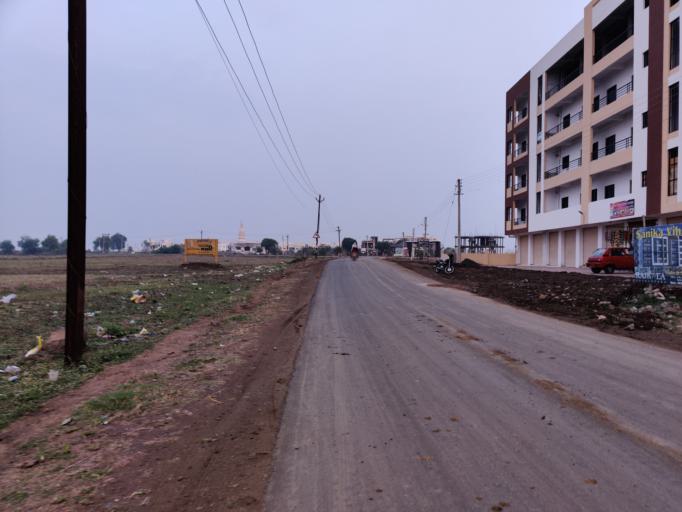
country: IN
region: Maharashtra
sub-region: Nagpur Division
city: Kamthi
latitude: 21.1959
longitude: 79.1517
